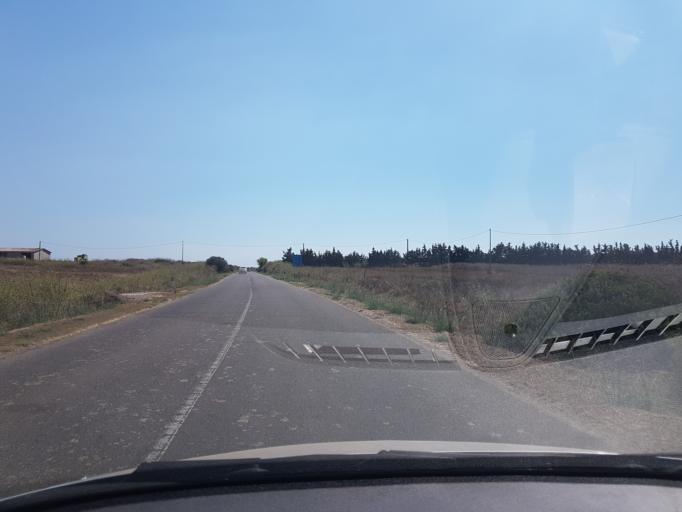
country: IT
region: Sardinia
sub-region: Provincia di Oristano
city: Nurachi
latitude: 39.9808
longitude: 8.4539
